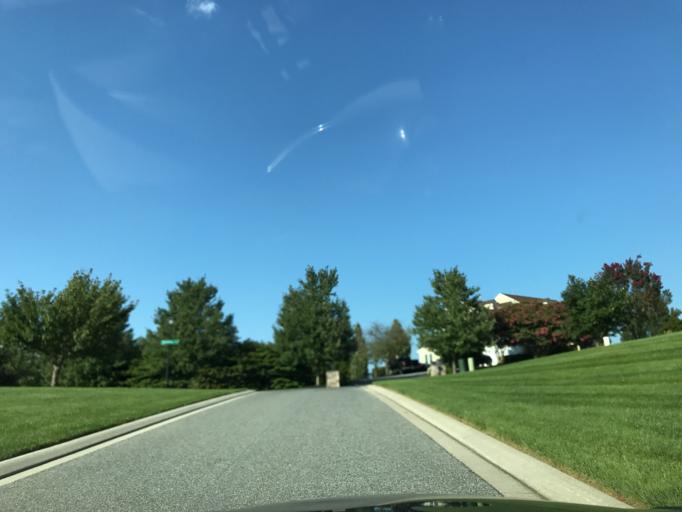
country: US
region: Maryland
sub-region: Baltimore County
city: Hunt Valley
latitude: 39.5273
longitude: -76.6163
